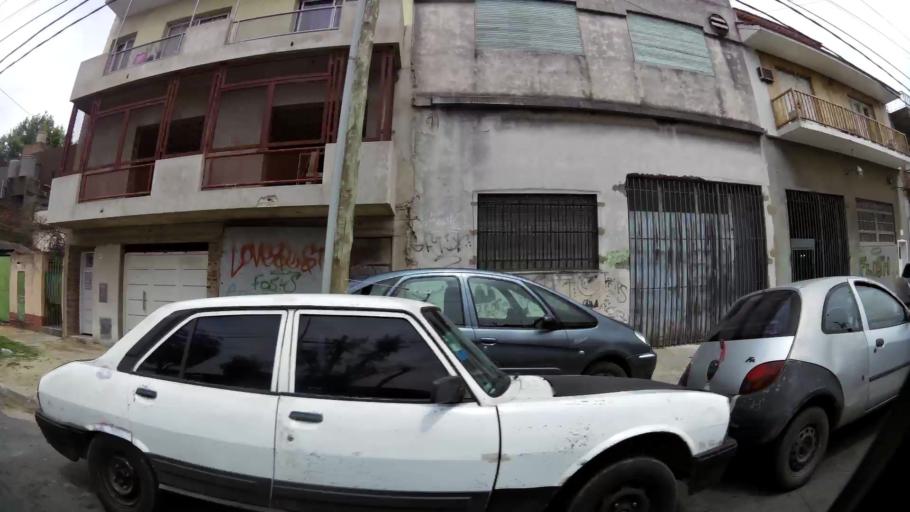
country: AR
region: Buenos Aires
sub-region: Partido de Avellaneda
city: Avellaneda
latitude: -34.6654
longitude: -58.3477
